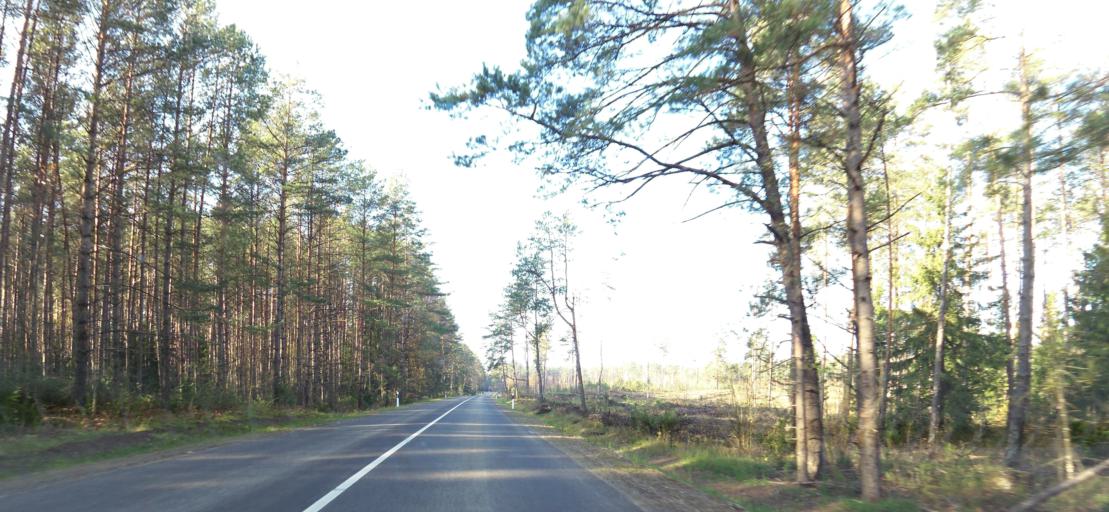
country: LT
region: Vilnius County
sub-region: Trakai
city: Rudiskes
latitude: 54.5106
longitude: 24.9169
